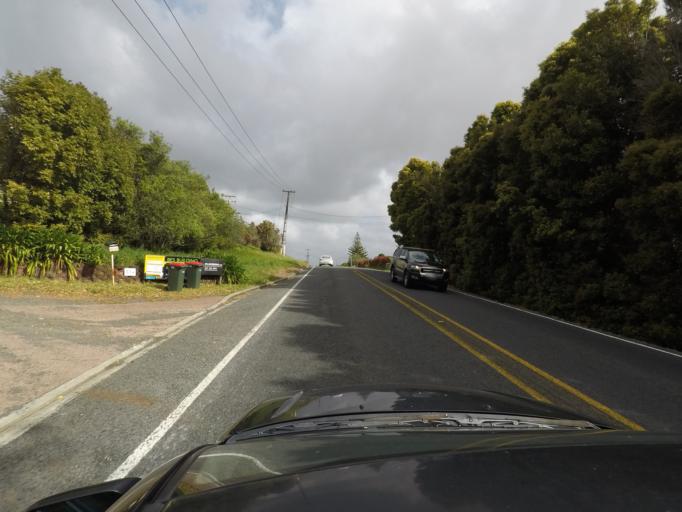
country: NZ
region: Auckland
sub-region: Auckland
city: Pakuranga
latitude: -36.9320
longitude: 174.9377
